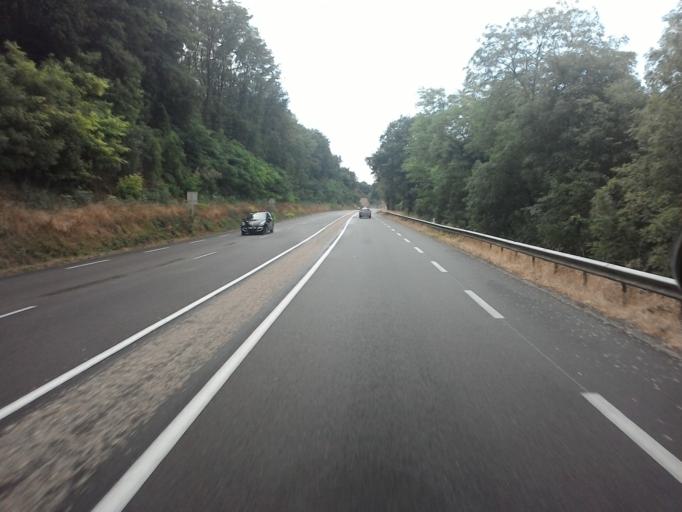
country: FR
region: Franche-Comte
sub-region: Departement du Jura
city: Bletterans
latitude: 46.7914
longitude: 5.5671
